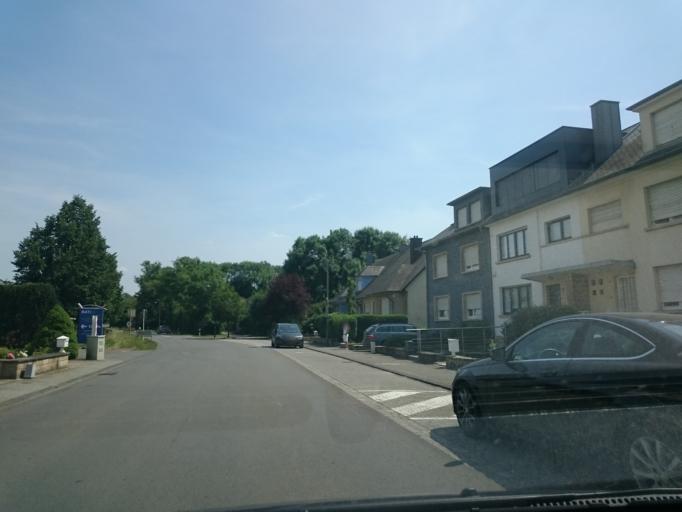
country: LU
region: Luxembourg
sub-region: Canton de Luxembourg
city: Strassen
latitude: 49.6167
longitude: 6.0789
